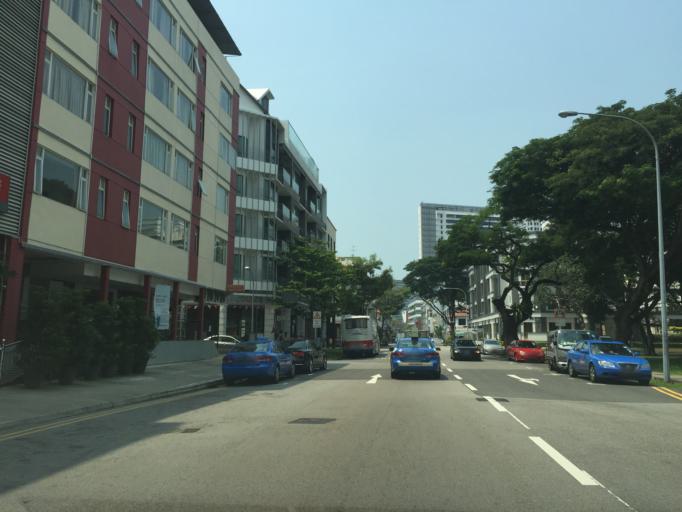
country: SG
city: Singapore
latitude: 1.3171
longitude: 103.8529
